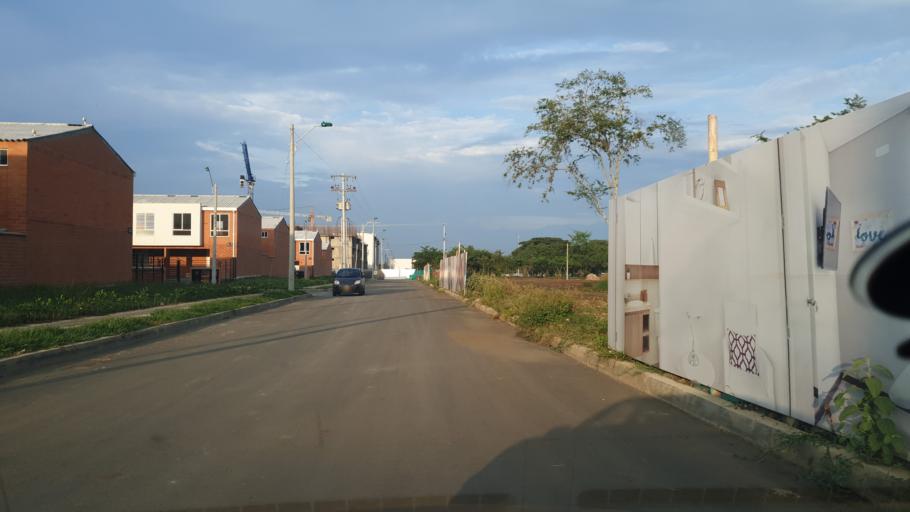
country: CO
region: Valle del Cauca
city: Jamundi
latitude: 3.3455
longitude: -76.5192
